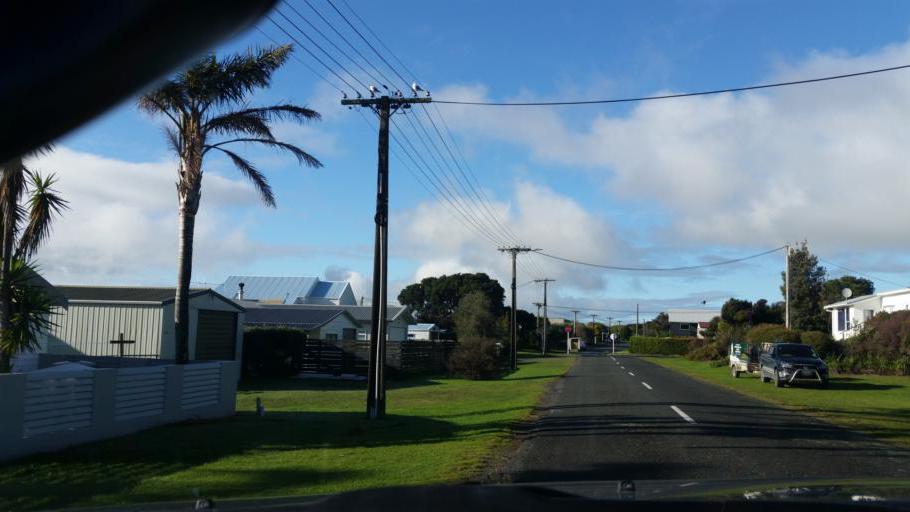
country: NZ
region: Auckland
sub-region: Auckland
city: Wellsford
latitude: -36.0895
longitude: 174.5881
